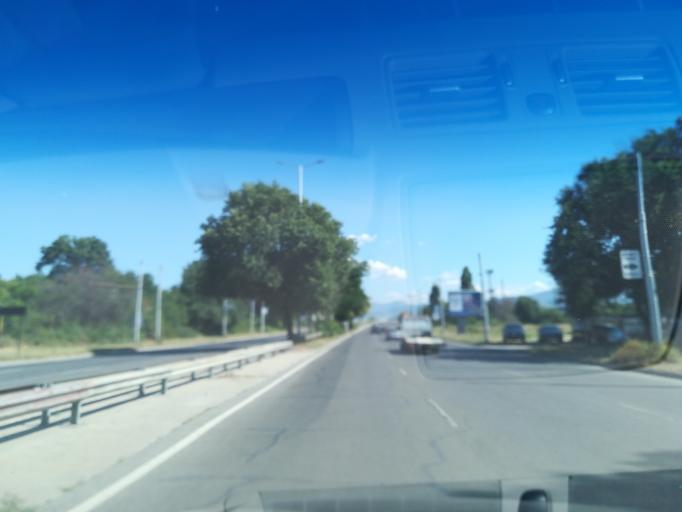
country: BG
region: Plovdiv
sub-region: Obshtina Plovdiv
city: Plovdiv
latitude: 42.1219
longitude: 24.7738
